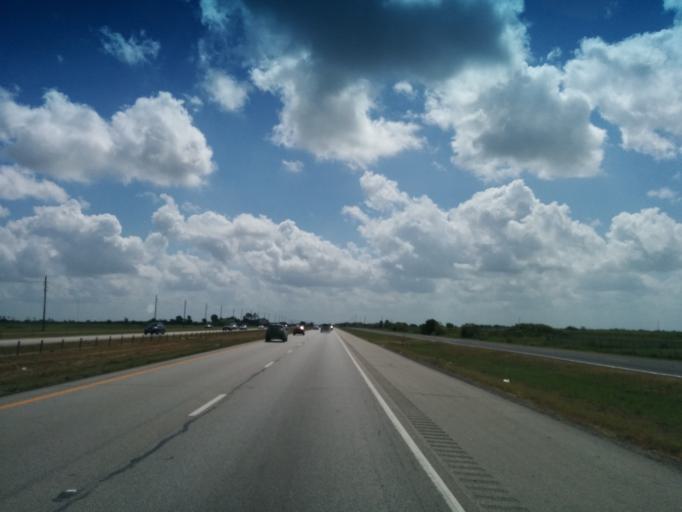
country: US
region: Texas
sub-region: Austin County
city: Sealy
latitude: 29.7543
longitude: -96.2538
